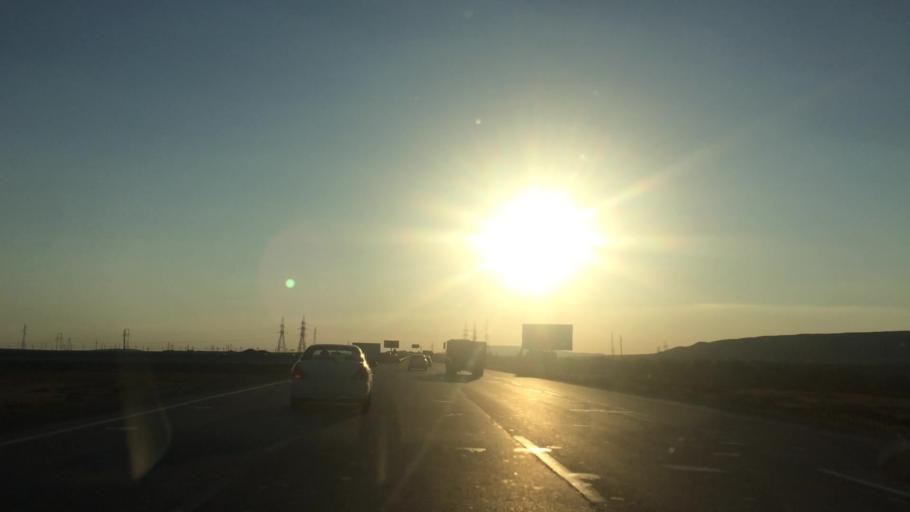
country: AZ
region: Baki
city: Qobustan
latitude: 39.9647
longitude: 49.4037
